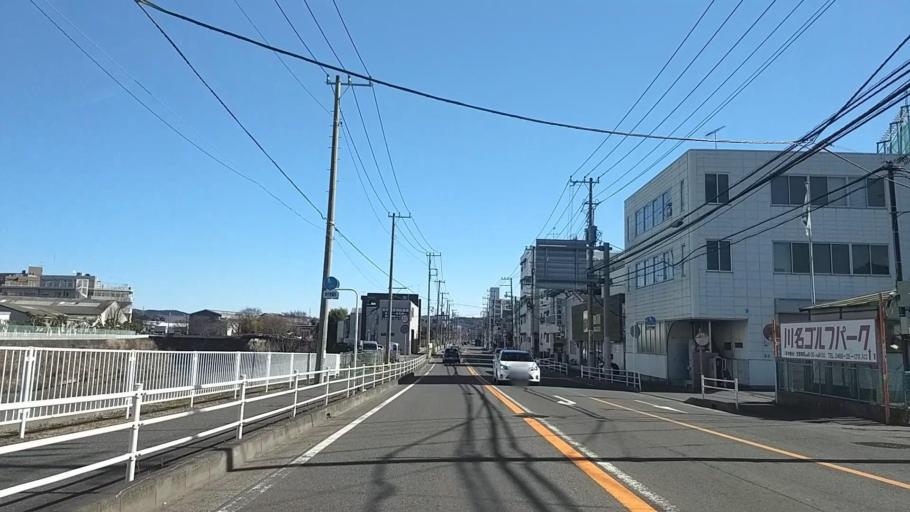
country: JP
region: Kanagawa
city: Fujisawa
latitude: 35.3326
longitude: 139.5007
